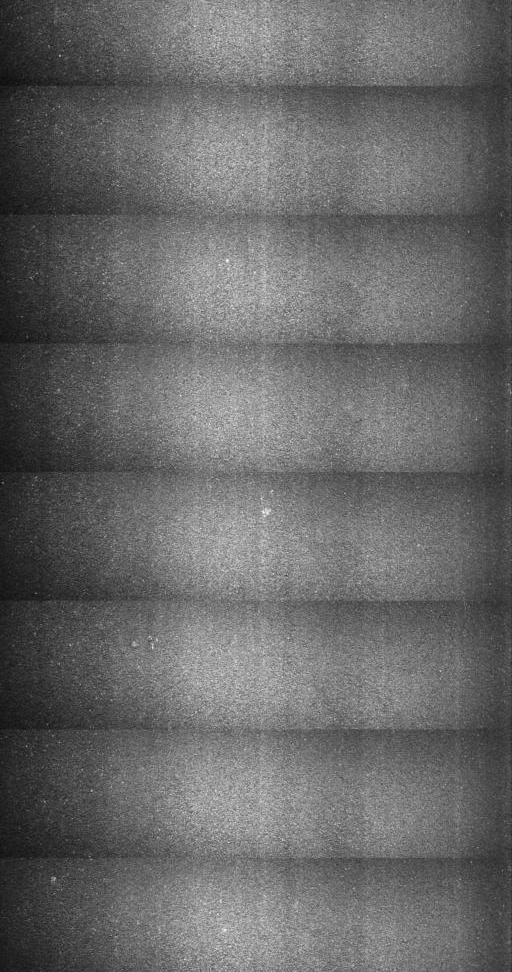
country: US
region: Vermont
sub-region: Franklin County
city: Richford
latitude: 44.9180
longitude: -72.6705
